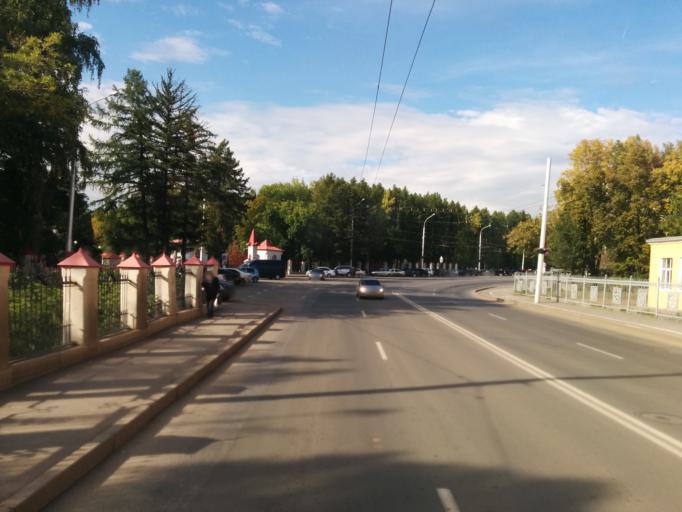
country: RU
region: Bashkortostan
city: Ufa
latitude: 54.8194
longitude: 56.0571
